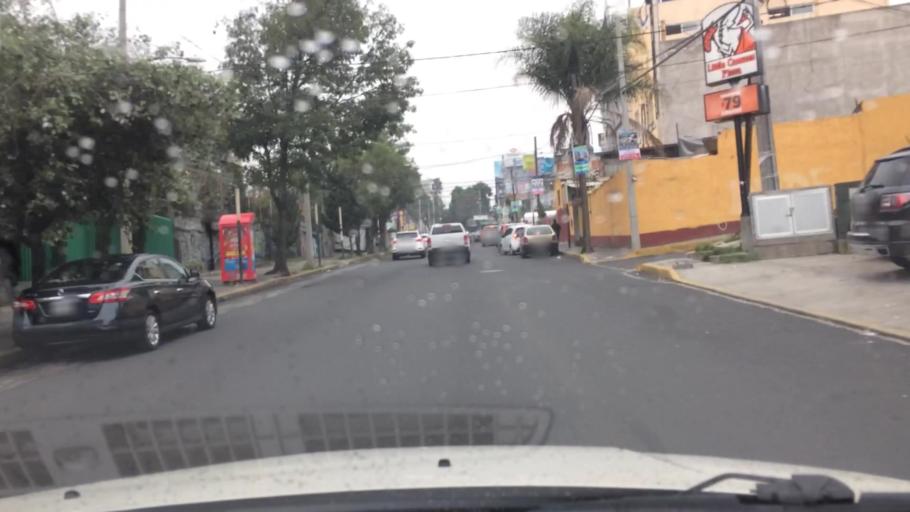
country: MX
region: Mexico City
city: Magdalena Contreras
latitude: 19.3410
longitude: -99.2086
